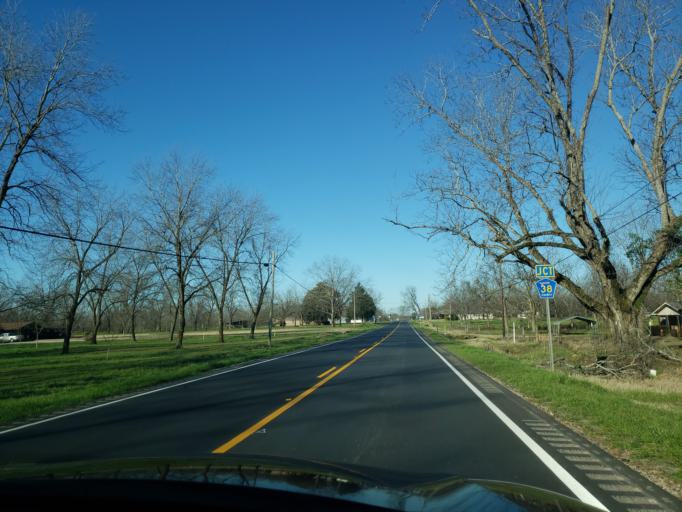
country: US
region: Alabama
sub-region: Macon County
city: Tuskegee
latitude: 32.5822
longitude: -85.7333
